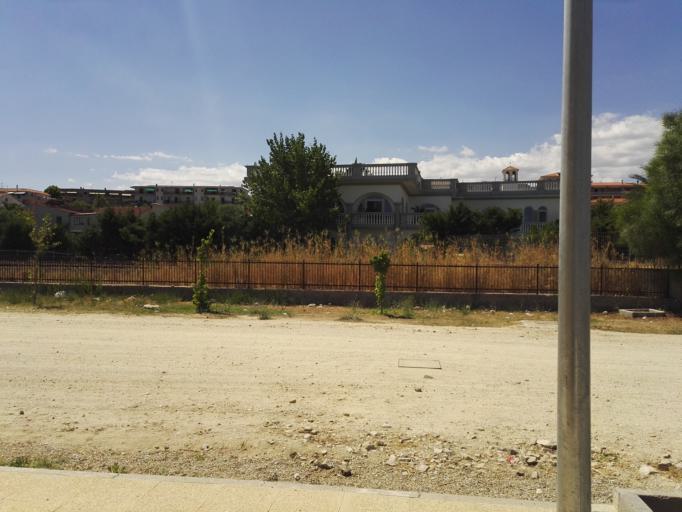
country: IT
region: Calabria
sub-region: Provincia di Catanzaro
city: Santa Caterina dello Ionio Marina
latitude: 38.5296
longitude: 16.5716
